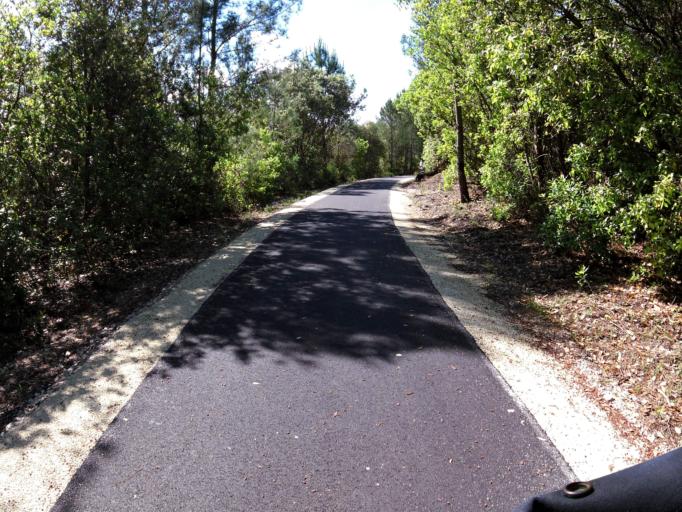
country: FR
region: Aquitaine
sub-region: Departement de la Gironde
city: Lacanau
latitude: 45.0314
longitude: -1.1762
